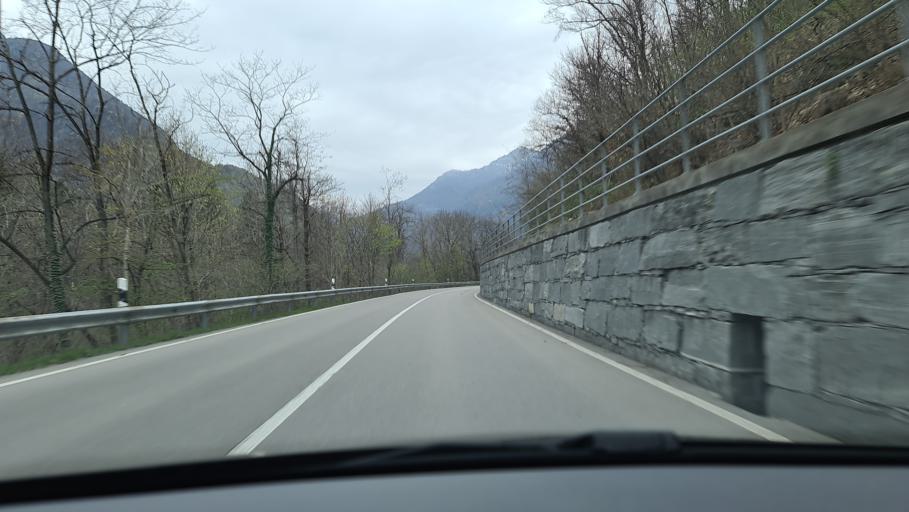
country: CH
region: Ticino
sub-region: Locarno District
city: Verscio
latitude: 46.2571
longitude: 8.6934
